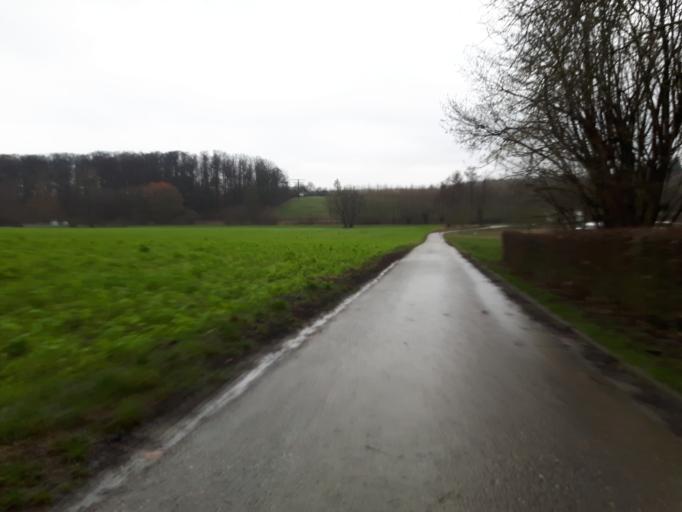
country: DE
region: Baden-Wuerttemberg
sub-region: Regierungsbezirk Stuttgart
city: Bad Rappenau
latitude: 49.2437
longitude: 9.1156
